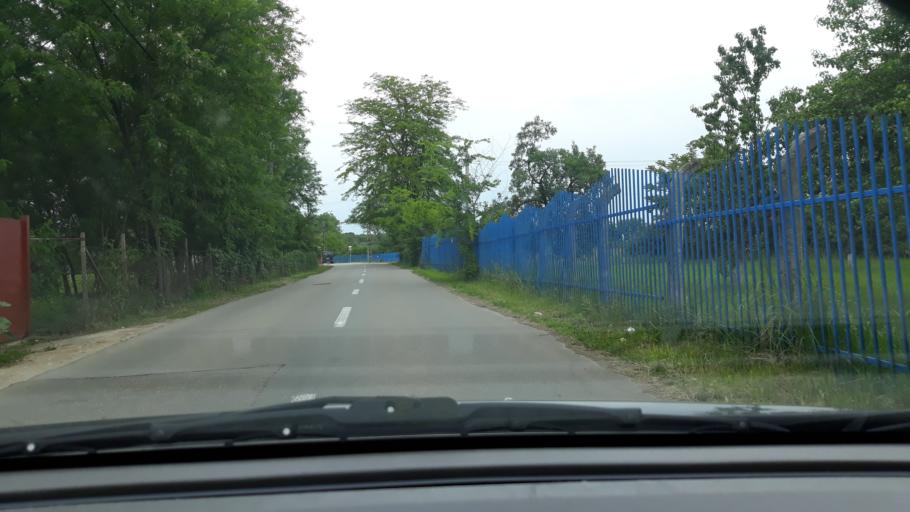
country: RO
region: Bihor
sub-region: Comuna Sanmartin
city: Sanmartin
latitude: 47.0498
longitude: 21.9844
